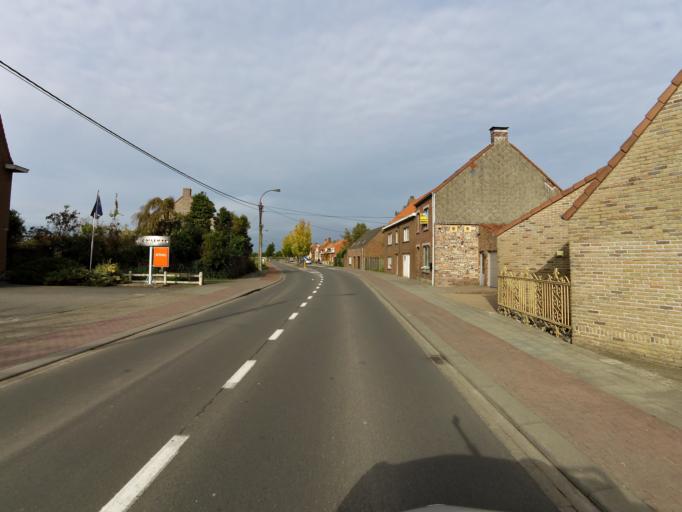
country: BE
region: Flanders
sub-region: Provincie West-Vlaanderen
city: Ichtegem
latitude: 51.1398
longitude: 3.0259
